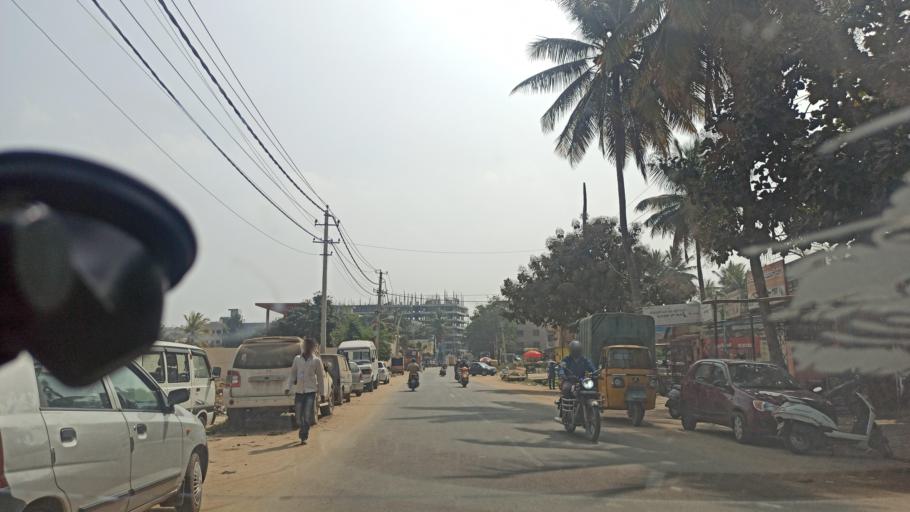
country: IN
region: Karnataka
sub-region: Bangalore Urban
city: Yelahanka
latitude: 13.0960
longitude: 77.6002
